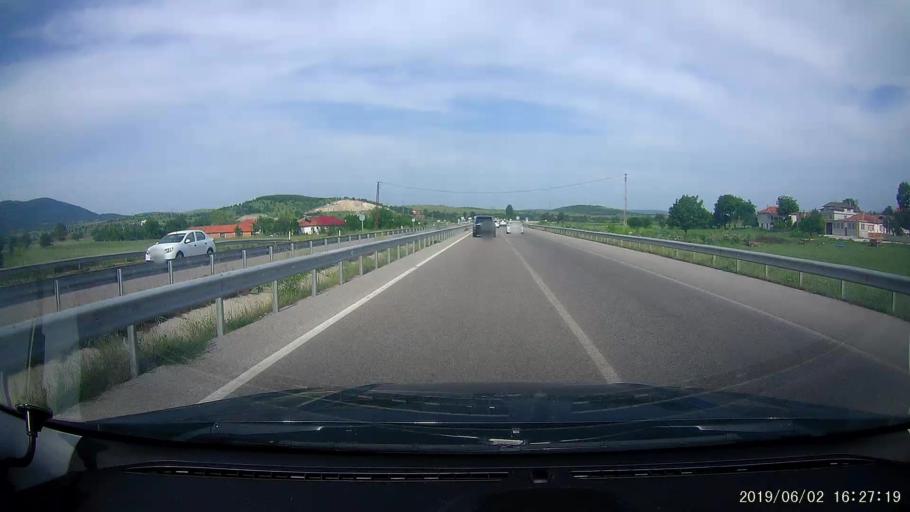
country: TR
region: Samsun
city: Ladik
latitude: 41.0018
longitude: 35.8243
